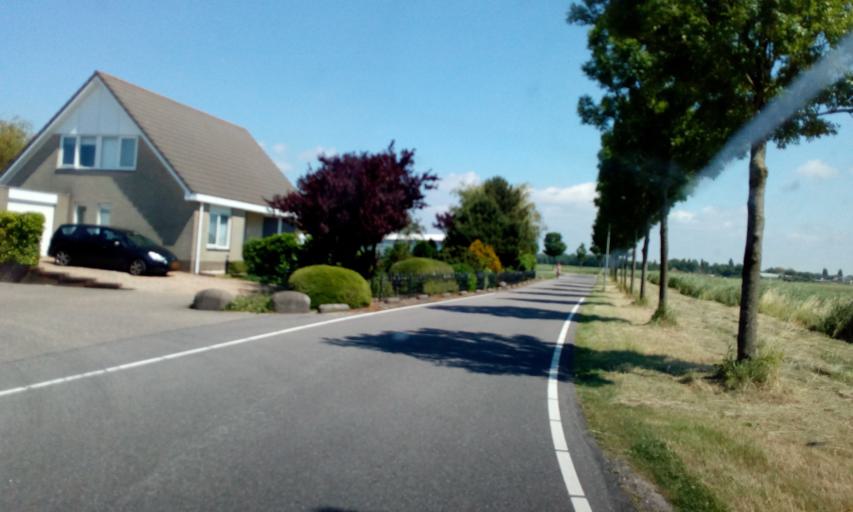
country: NL
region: South Holland
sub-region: Gemeente Westland
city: De Lier
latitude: 51.9778
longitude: 4.2959
